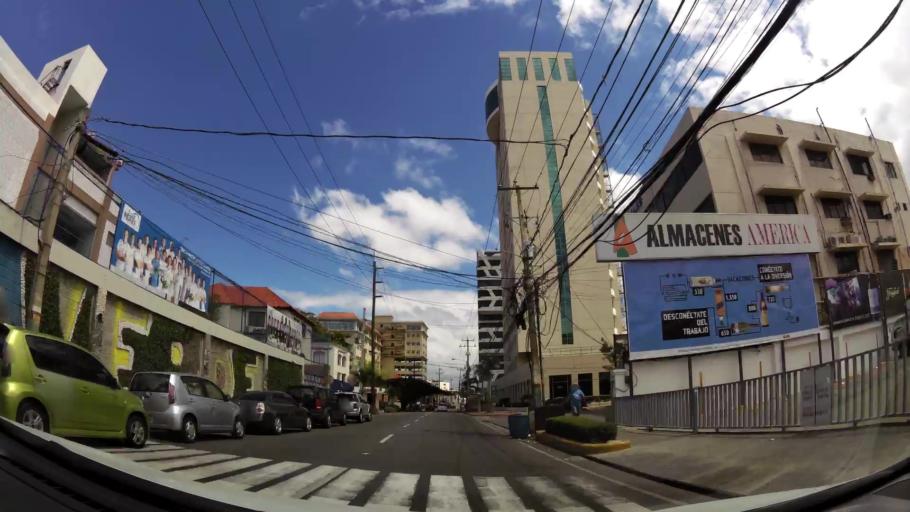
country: DO
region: Nacional
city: La Julia
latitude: 18.4742
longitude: -69.9367
